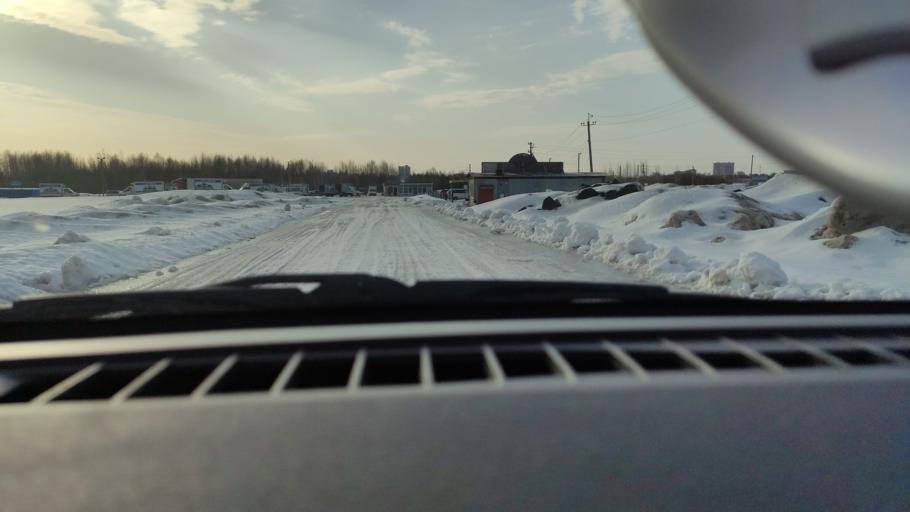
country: RU
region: Perm
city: Perm
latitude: 58.0379
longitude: 56.2022
